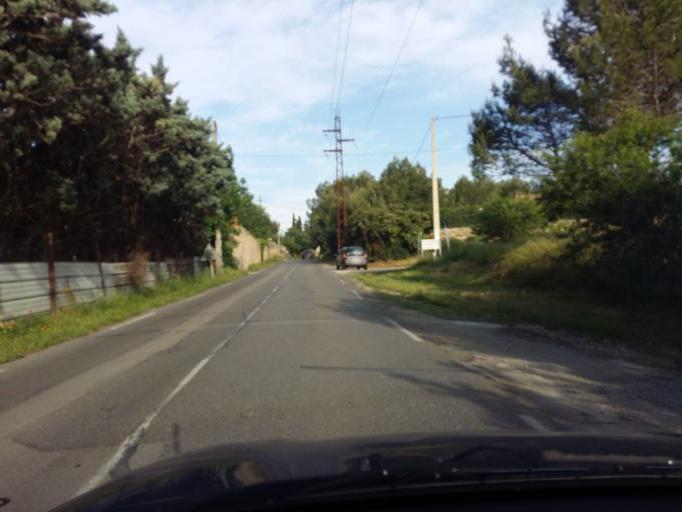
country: FR
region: Provence-Alpes-Cote d'Azur
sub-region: Departement des Bouches-du-Rhone
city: Salon-de-Provence
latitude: 43.6368
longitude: 5.1231
